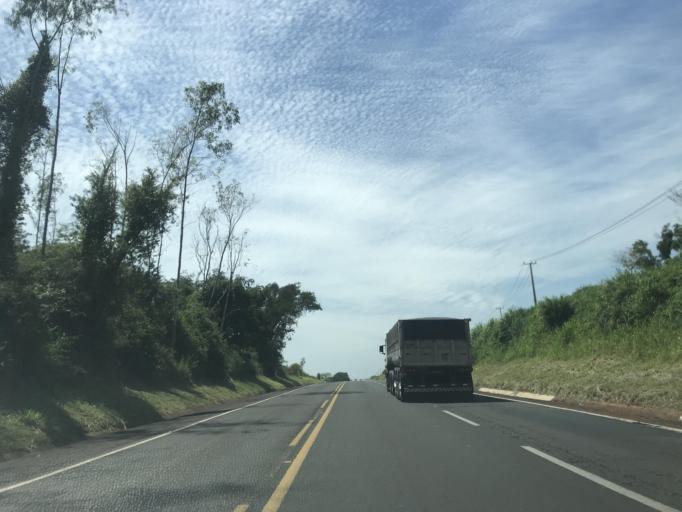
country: BR
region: Parana
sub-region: Paranavai
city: Nova Aurora
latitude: -22.9632
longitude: -52.6428
